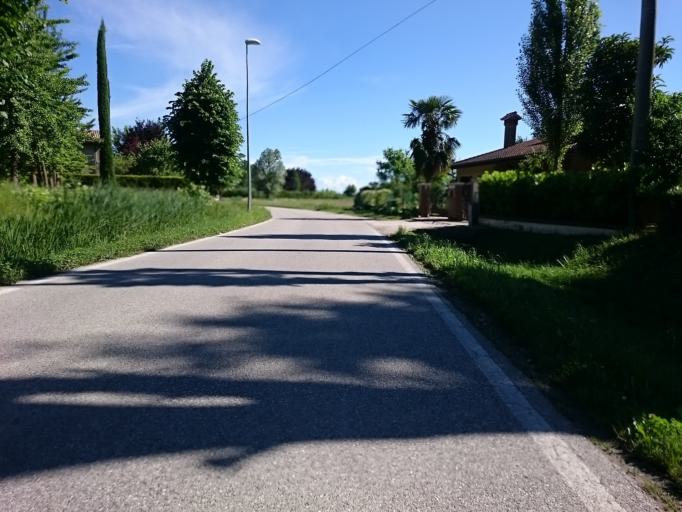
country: IT
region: Veneto
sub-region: Provincia di Padova
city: Legnaro
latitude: 45.3555
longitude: 11.9725
